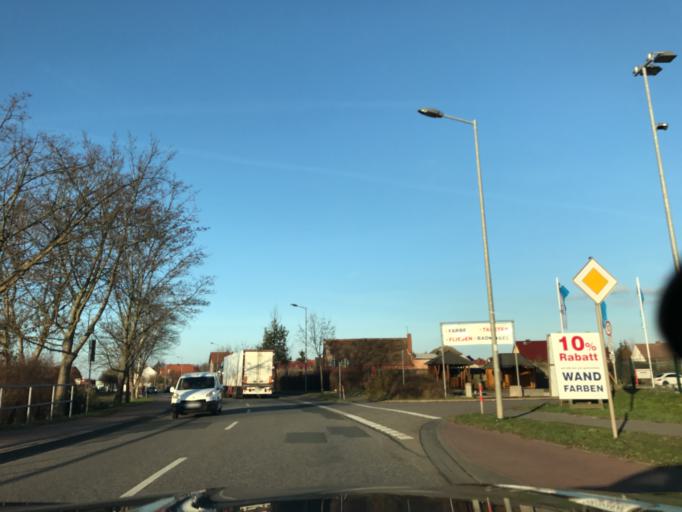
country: DE
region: Saxony-Anhalt
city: Burg bei Magdeburg
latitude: 52.2618
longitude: 11.8638
